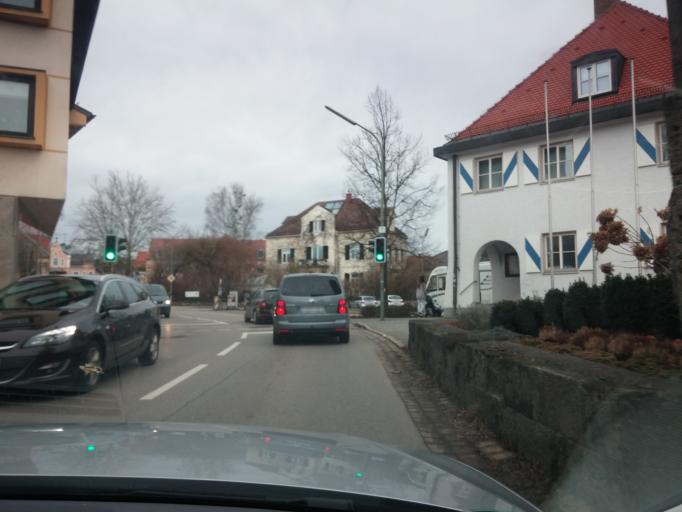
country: DE
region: Bavaria
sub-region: Upper Bavaria
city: Glonn
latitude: 47.9875
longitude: 11.8662
